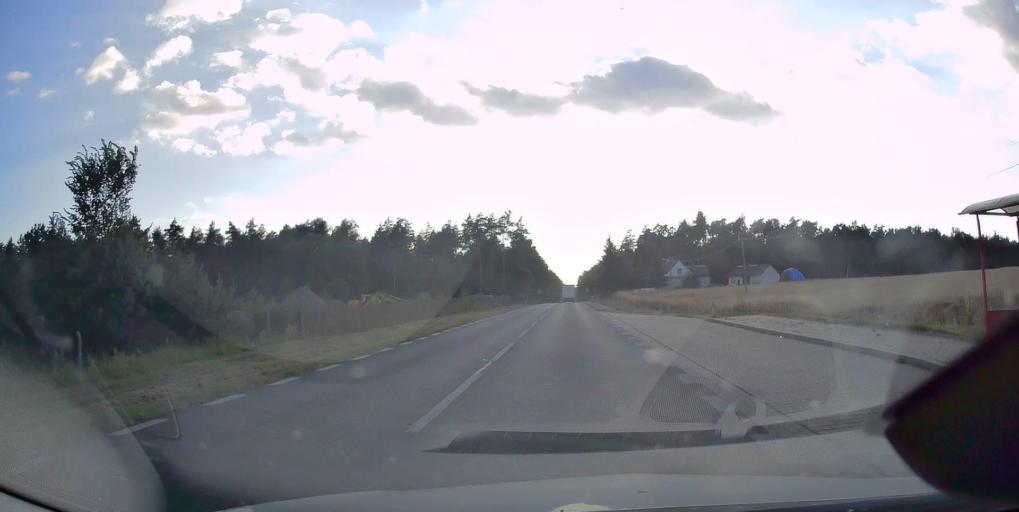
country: PL
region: Lodz Voivodeship
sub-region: Powiat rawski
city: Biala Rawska
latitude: 51.8005
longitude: 20.4244
